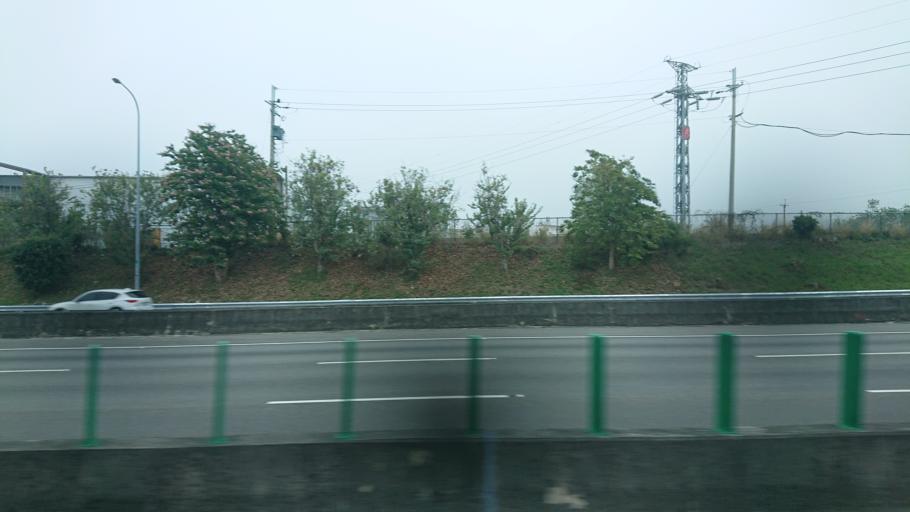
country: TW
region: Taiwan
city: Fengyuan
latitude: 24.3268
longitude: 120.7121
